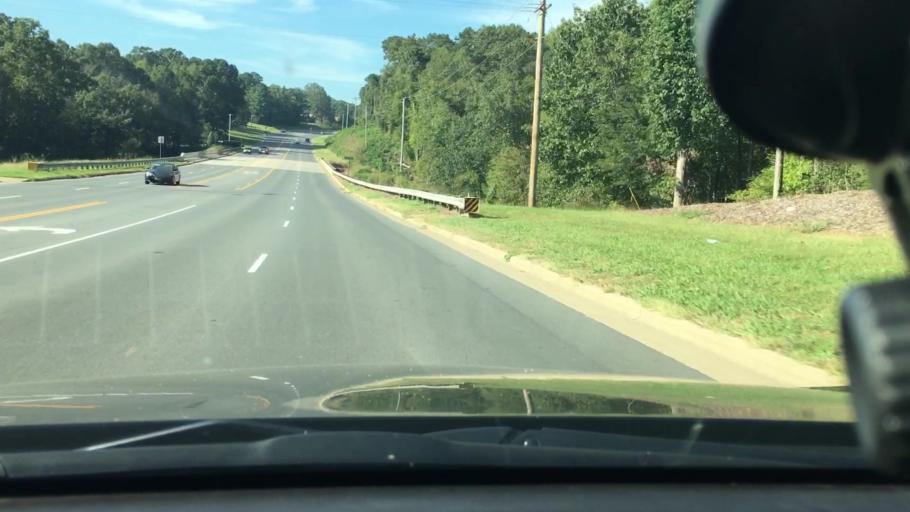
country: US
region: North Carolina
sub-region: Stanly County
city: Albemarle
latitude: 35.3386
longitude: -80.2169
